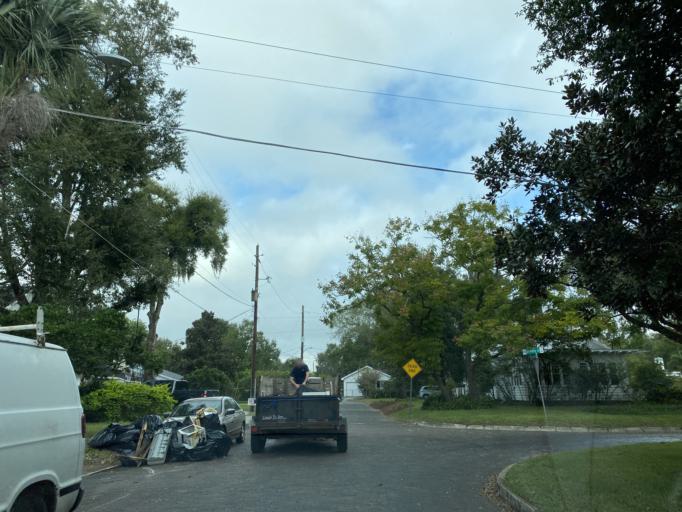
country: US
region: Florida
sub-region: Orange County
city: Orlando
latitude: 28.5633
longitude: -81.3883
